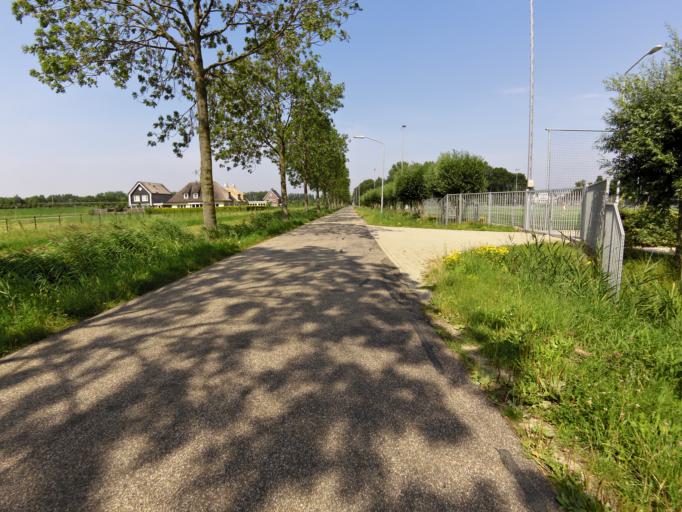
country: NL
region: South Holland
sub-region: Gemeente Dordrecht
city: Dordrecht
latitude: 51.7726
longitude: 4.6627
